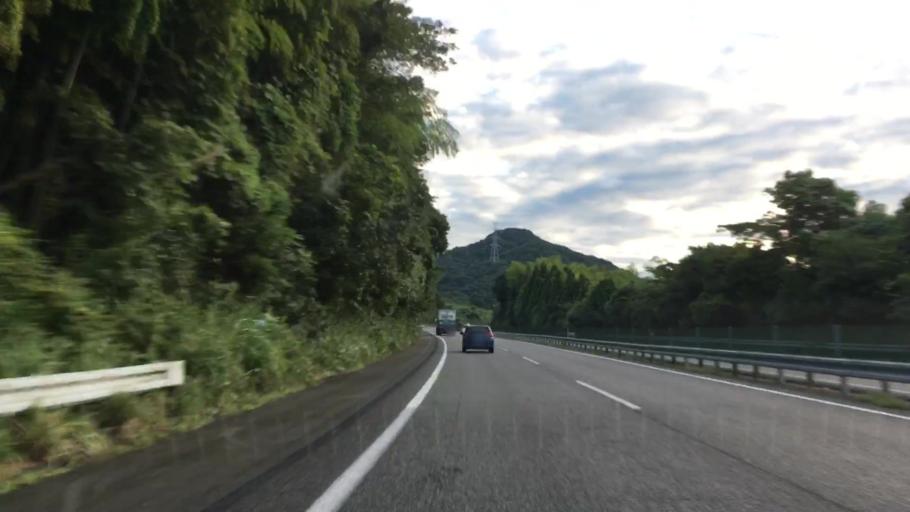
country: JP
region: Yamaguchi
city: Shimonoseki
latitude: 34.0435
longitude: 130.9875
